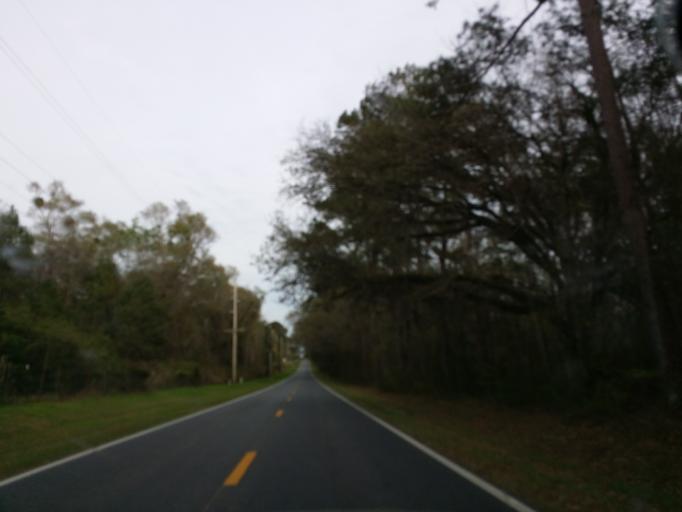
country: US
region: Florida
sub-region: Leon County
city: Tallahassee
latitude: 30.5365
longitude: -84.1460
